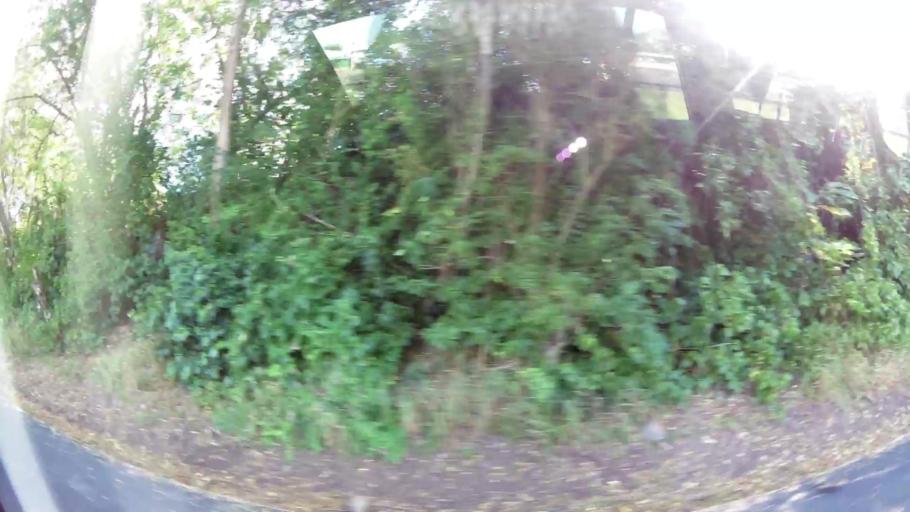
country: LC
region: Castries Quarter
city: Bisee
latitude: 14.0191
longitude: -60.9947
